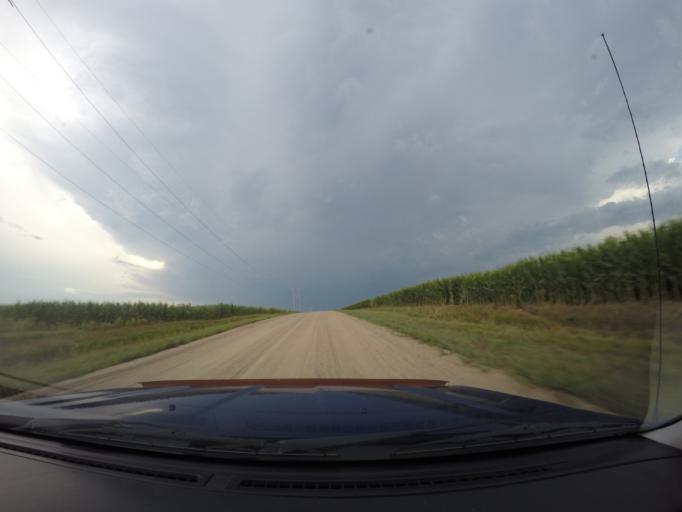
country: US
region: Nebraska
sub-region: Buffalo County
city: Kearney
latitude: 40.8443
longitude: -99.1089
